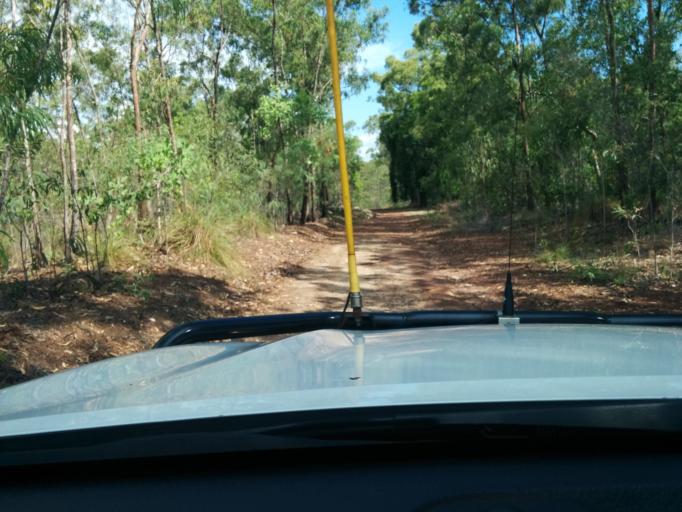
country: AU
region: Northern Territory
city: Alyangula
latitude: -13.8440
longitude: 136.4185
